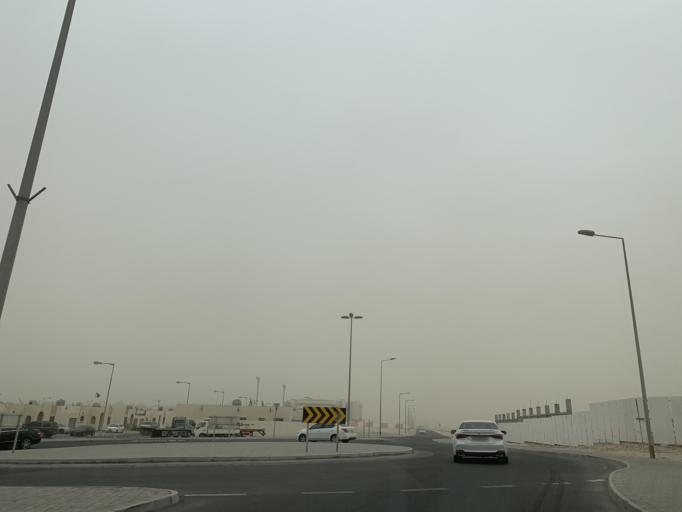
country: BH
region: Central Governorate
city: Madinat Hamad
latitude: 26.1360
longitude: 50.5189
